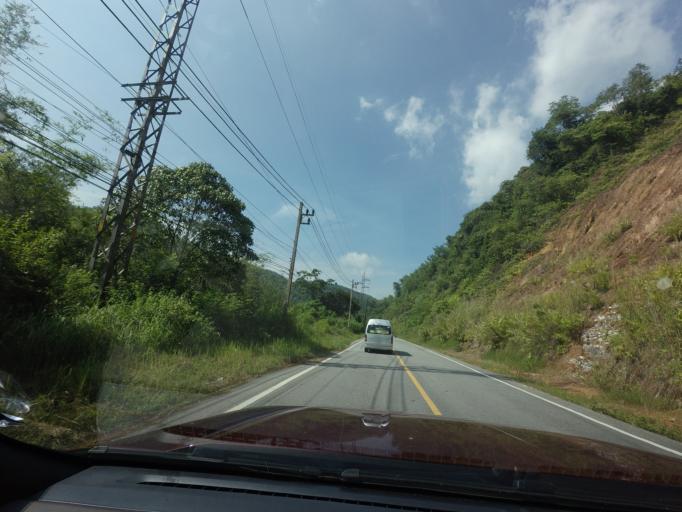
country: TH
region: Yala
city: Betong
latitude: 5.9320
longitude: 101.1859
